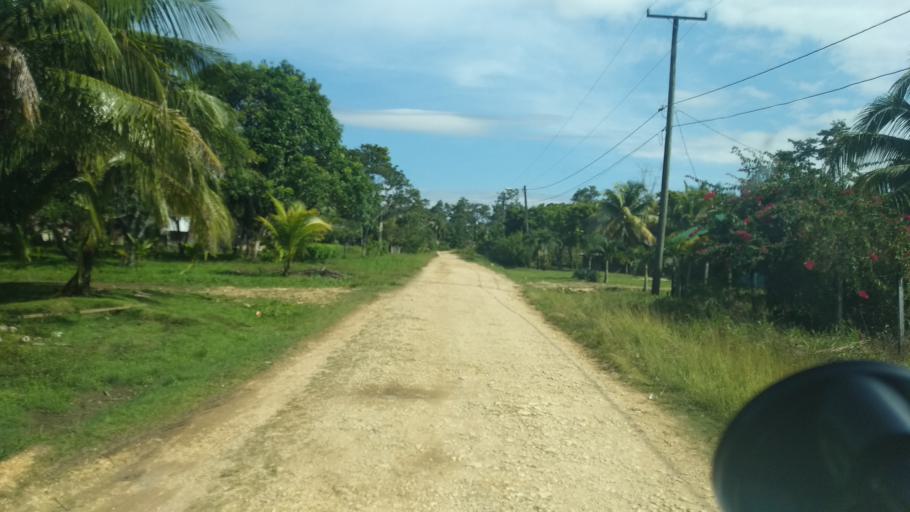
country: BZ
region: Toledo
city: Punta Gorda
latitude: 16.2172
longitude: -88.9028
